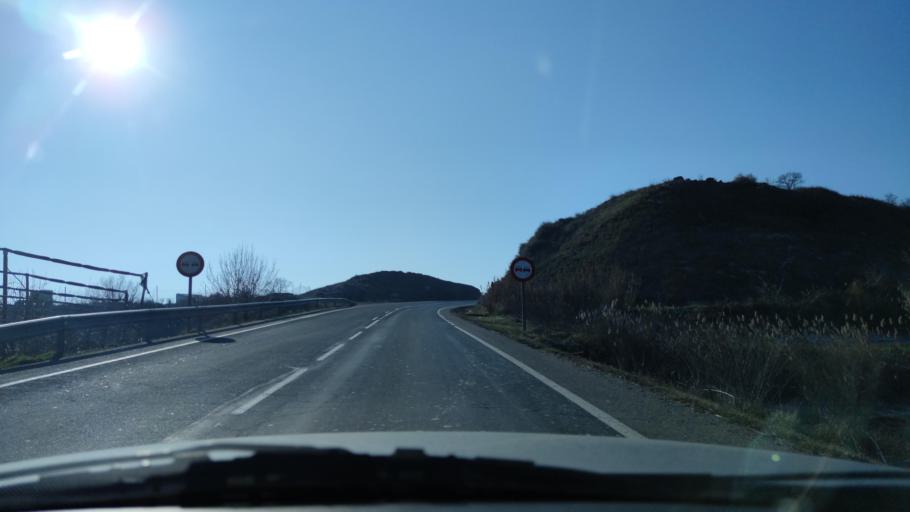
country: ES
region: Catalonia
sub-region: Provincia de Lleida
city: Torrefarrera
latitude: 41.7035
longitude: 0.6367
